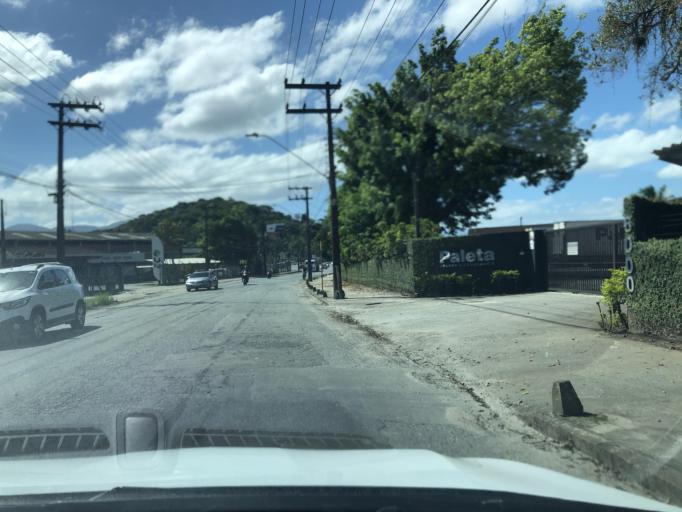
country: BR
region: Santa Catarina
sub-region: Joinville
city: Joinville
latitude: -26.2601
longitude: -48.8659
